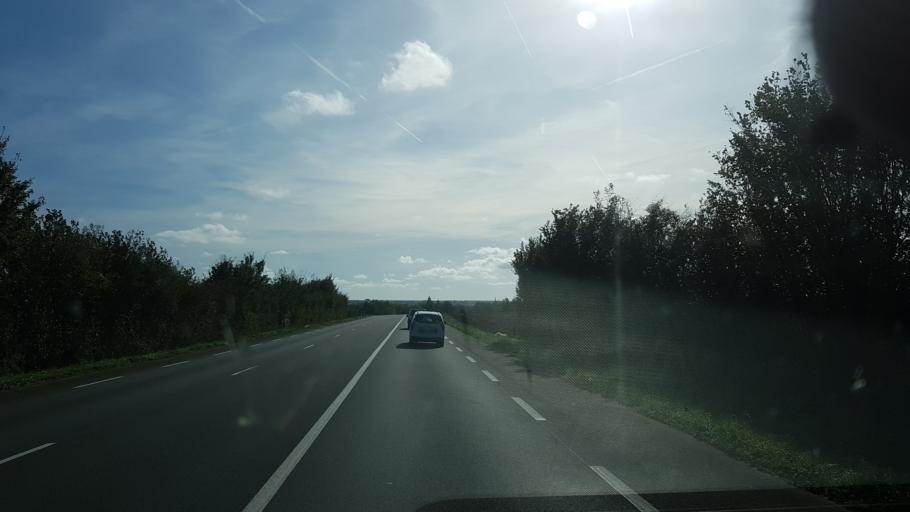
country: FR
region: Poitou-Charentes
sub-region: Departement de la Charente
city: Chasseneuil-sur-Bonnieure
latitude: 45.8495
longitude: 0.4622
